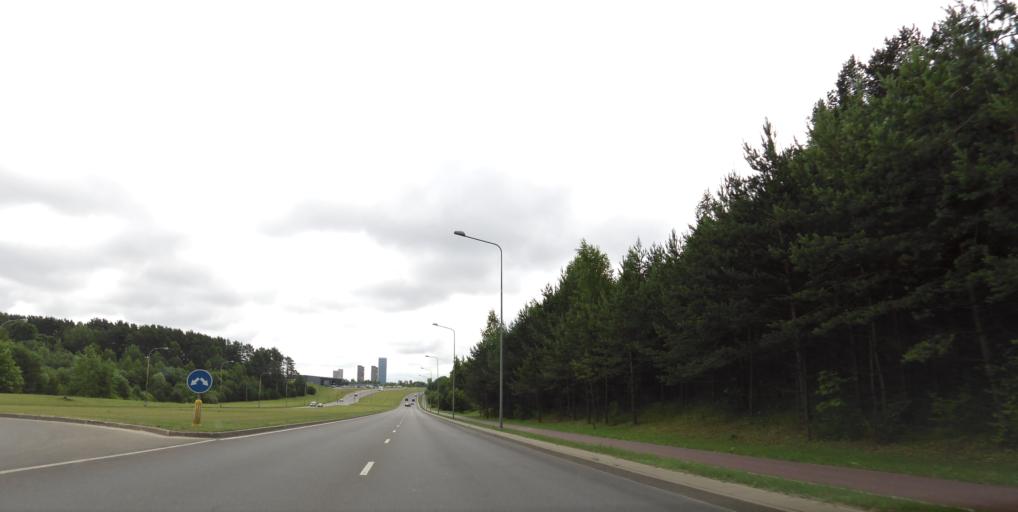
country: LT
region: Vilnius County
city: Pilaite
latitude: 54.7076
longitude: 25.1918
